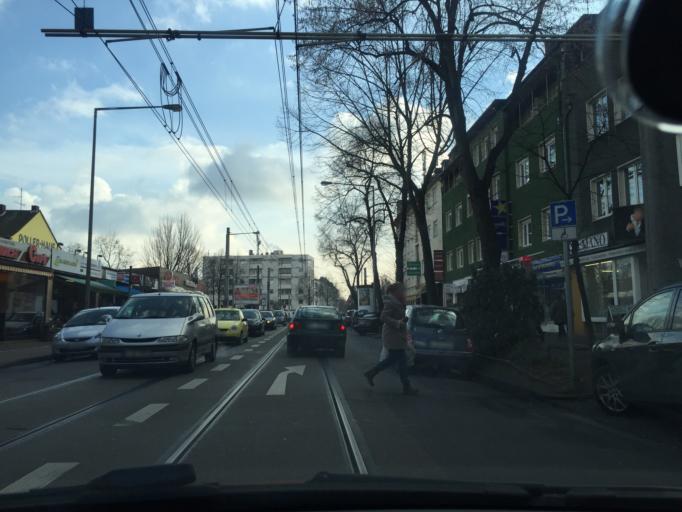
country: DE
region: North Rhine-Westphalia
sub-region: Regierungsbezirk Koln
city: Poll
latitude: 50.9166
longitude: 6.9906
